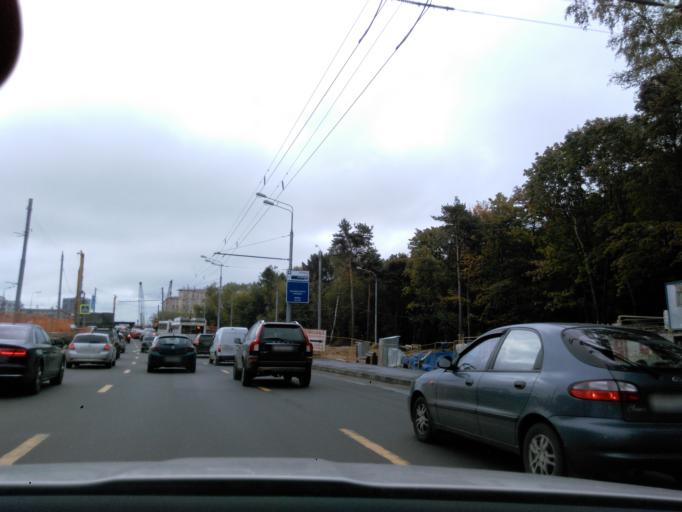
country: RU
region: Moscow
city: Pokrovskoye-Streshnevo
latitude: 55.8108
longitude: 37.4850
